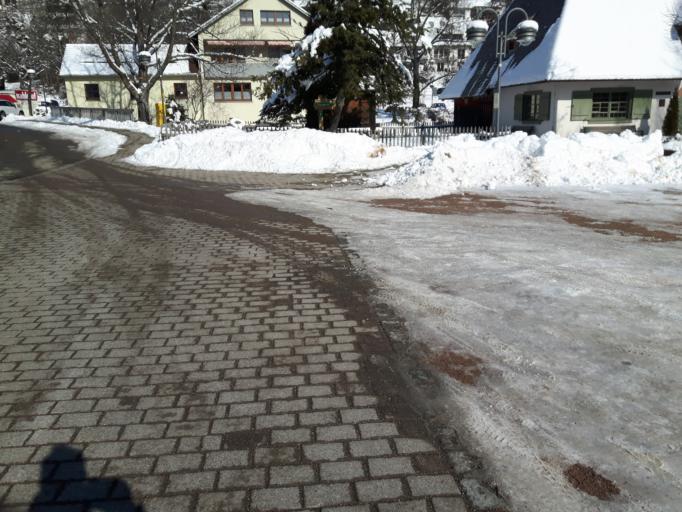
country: DE
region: Baden-Wuerttemberg
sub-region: Freiburg Region
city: Unterkirnach
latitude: 48.0780
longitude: 8.3655
